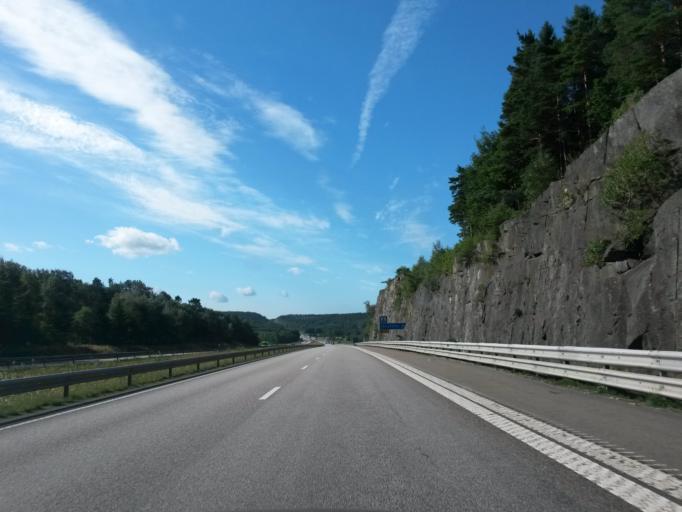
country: SE
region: Halland
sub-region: Kungsbacka Kommun
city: Frillesas
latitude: 57.3332
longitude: 12.2057
